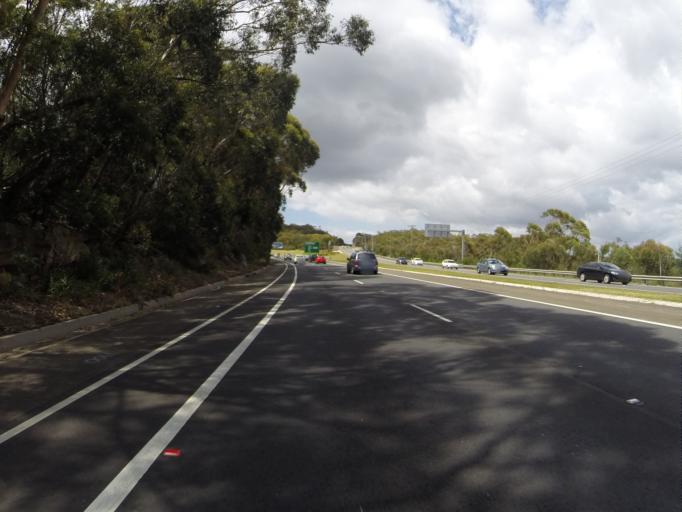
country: AU
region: New South Wales
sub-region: Wollongong
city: Helensburgh
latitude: -34.1389
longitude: 150.9941
